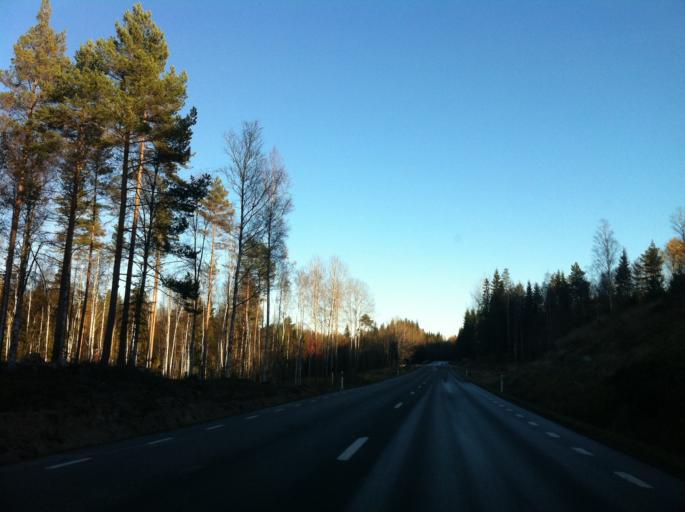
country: SE
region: Dalarna
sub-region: Faluns Kommun
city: Bjursas
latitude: 60.7411
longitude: 15.4088
